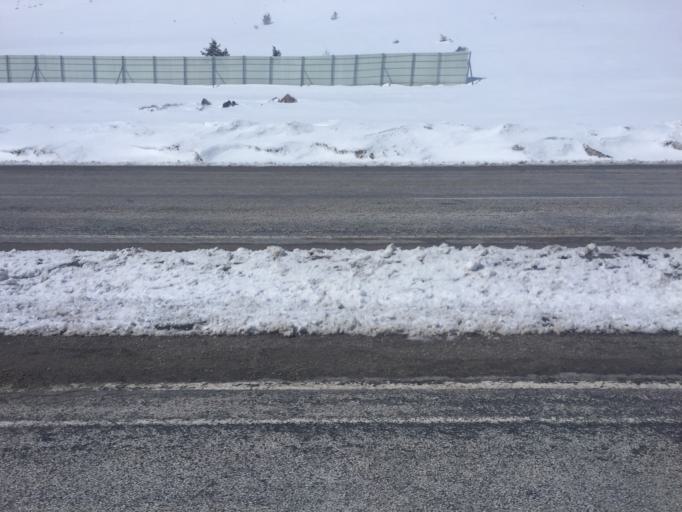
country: TR
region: Kahramanmaras
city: Goksun
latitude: 38.1886
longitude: 36.4568
